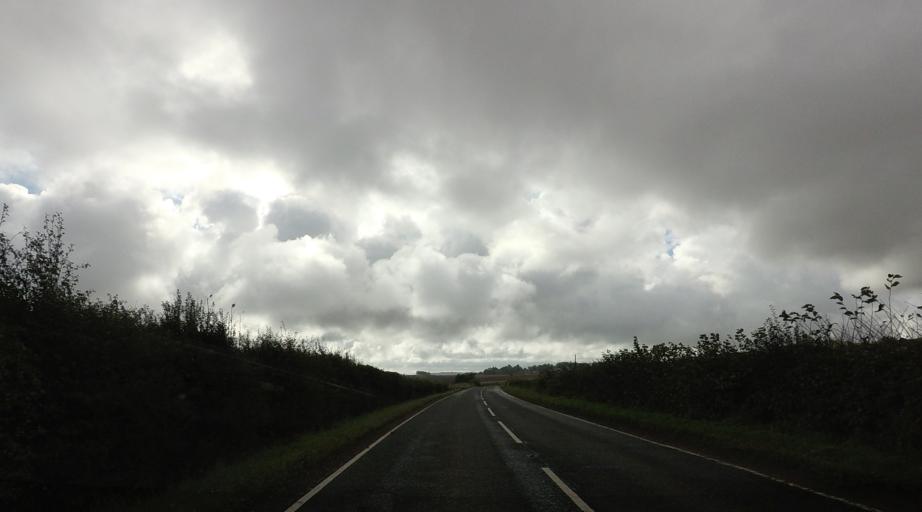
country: GB
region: Scotland
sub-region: Fife
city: Balmullo
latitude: 56.3683
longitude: -2.9326
